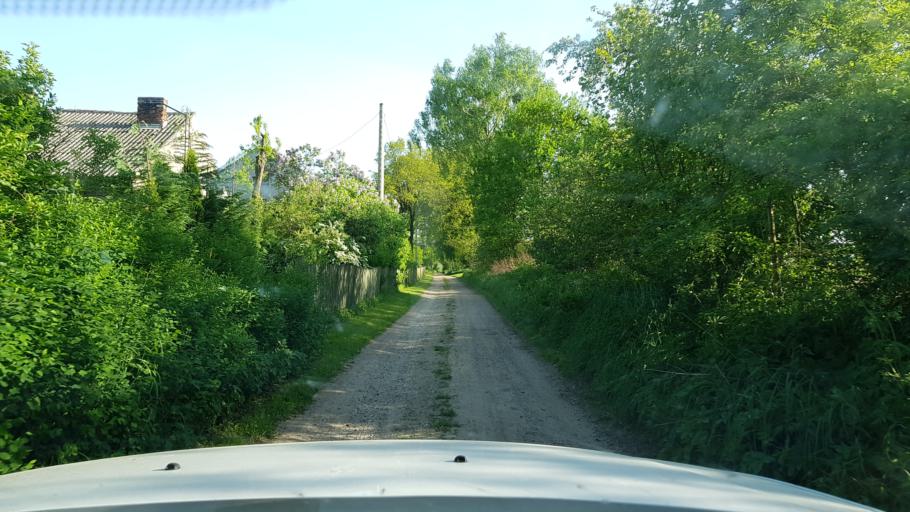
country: PL
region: West Pomeranian Voivodeship
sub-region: Powiat lobeski
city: Resko
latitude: 53.6929
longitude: 15.3359
